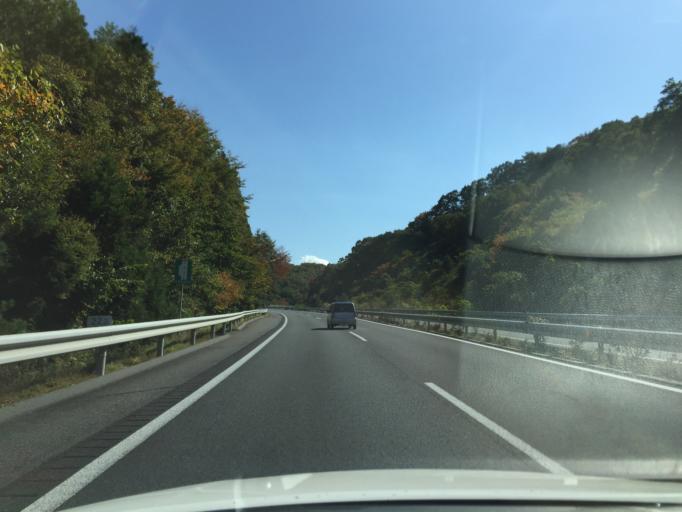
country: JP
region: Fukushima
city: Iwaki
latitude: 37.2022
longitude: 140.6959
